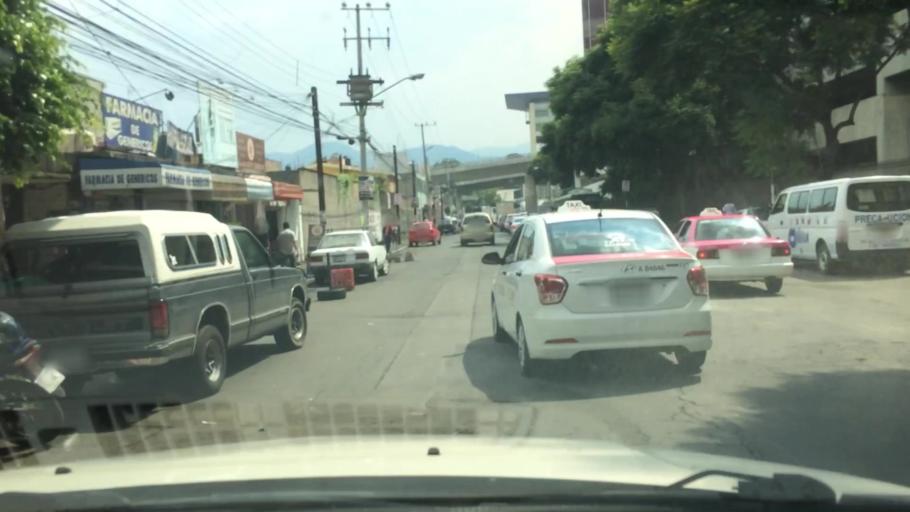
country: MX
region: Mexico City
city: Tlalpan
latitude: 19.2884
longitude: -99.1481
